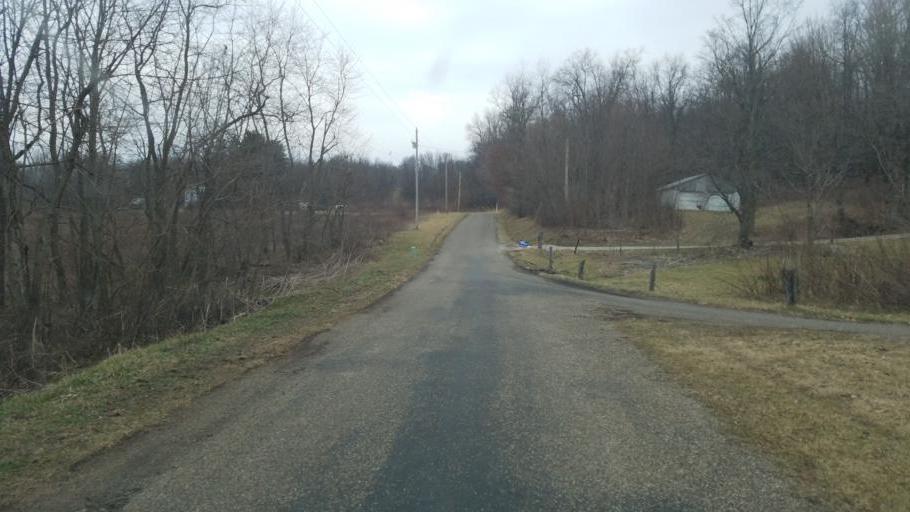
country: US
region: Ohio
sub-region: Ashland County
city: Loudonville
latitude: 40.7121
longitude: -82.3133
